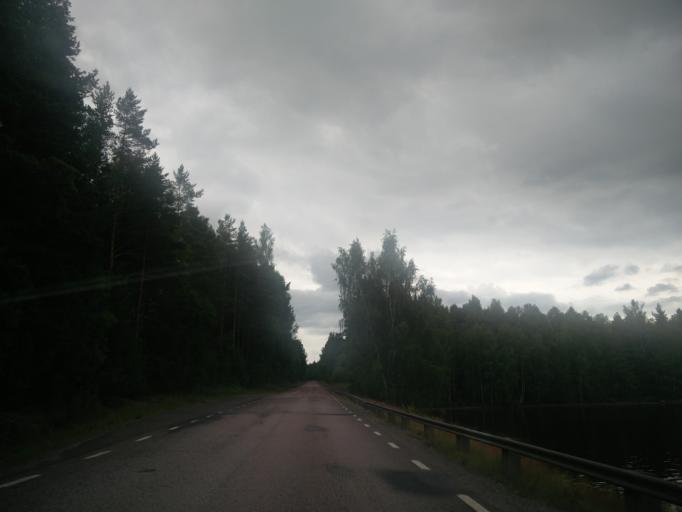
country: SE
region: Vaermland
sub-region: Arvika Kommun
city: Arvika
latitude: 59.9111
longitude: 12.6427
